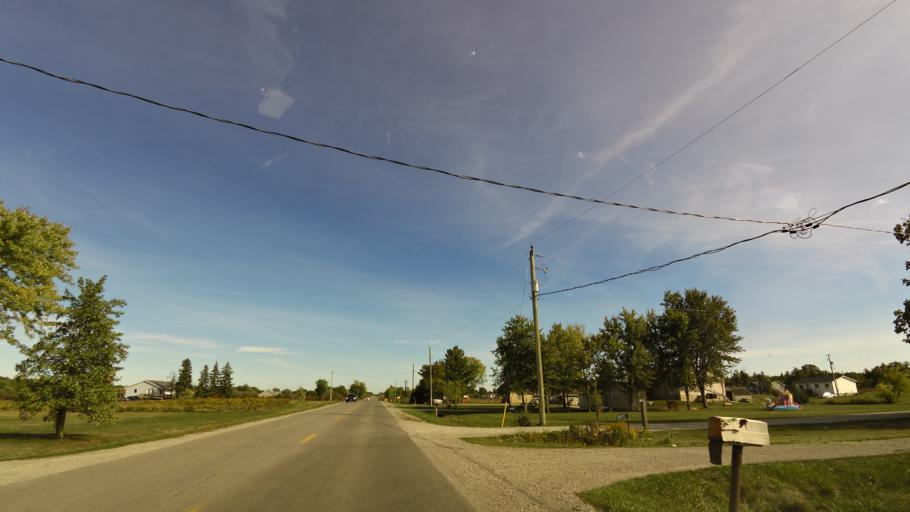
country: CA
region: Ontario
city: Ancaster
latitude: 43.0364
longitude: -80.0303
